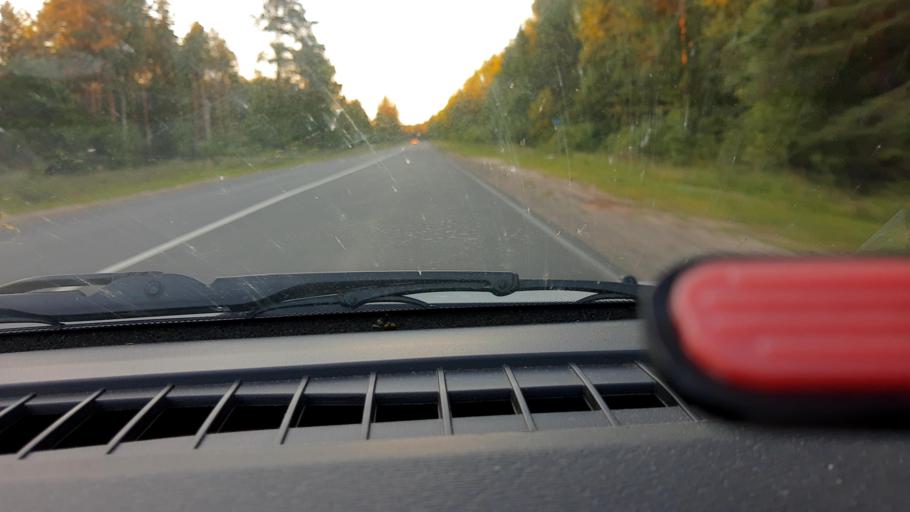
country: RU
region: Nizjnij Novgorod
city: Uren'
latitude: 57.3886
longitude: 45.6864
